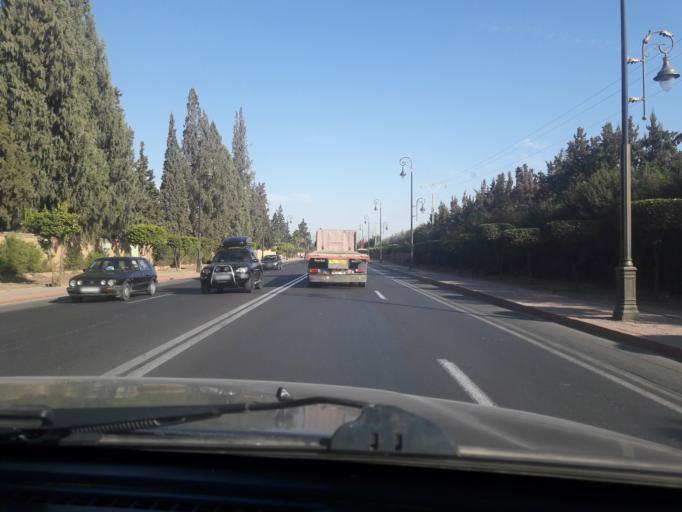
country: MA
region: Marrakech-Tensift-Al Haouz
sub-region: Marrakech
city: Marrakesh
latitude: 31.6483
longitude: -7.9600
